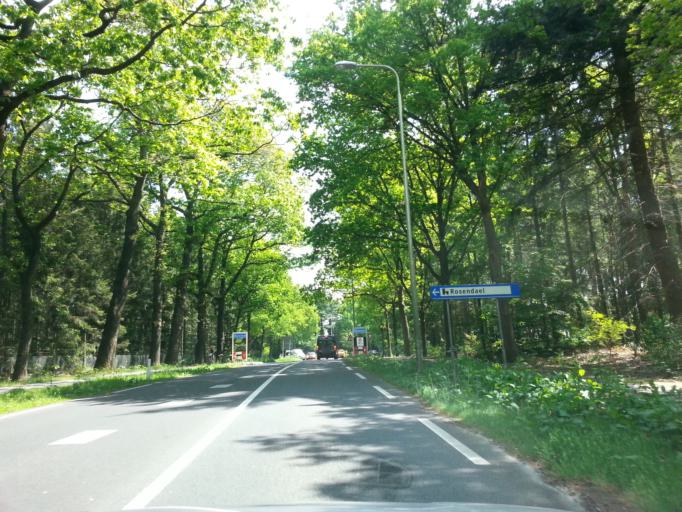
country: NL
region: Gelderland
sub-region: Gemeente Rozendaal
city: Rozendaal
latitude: 52.0077
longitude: 5.9578
